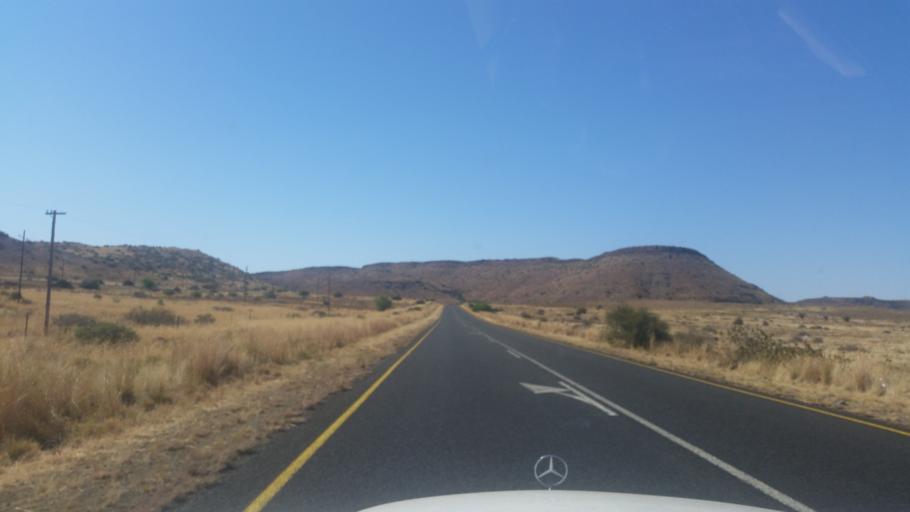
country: ZA
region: Orange Free State
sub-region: Xhariep District Municipality
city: Trompsburg
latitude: -30.5075
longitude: 26.0174
